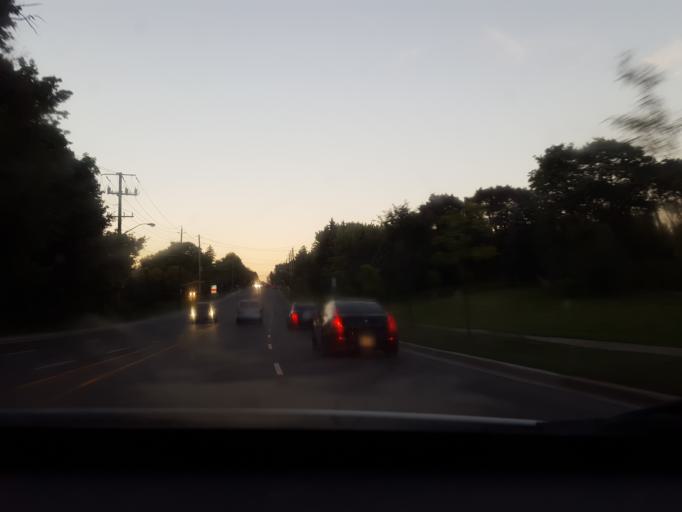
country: CA
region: Ontario
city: Willowdale
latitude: 43.7488
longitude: -79.3842
